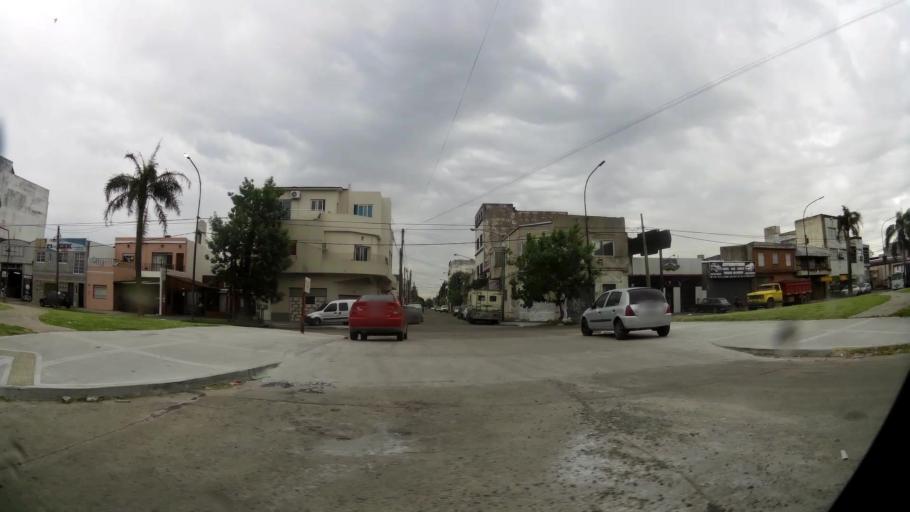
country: AR
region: Buenos Aires
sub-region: Partido de Lanus
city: Lanus
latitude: -34.6849
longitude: -58.3994
